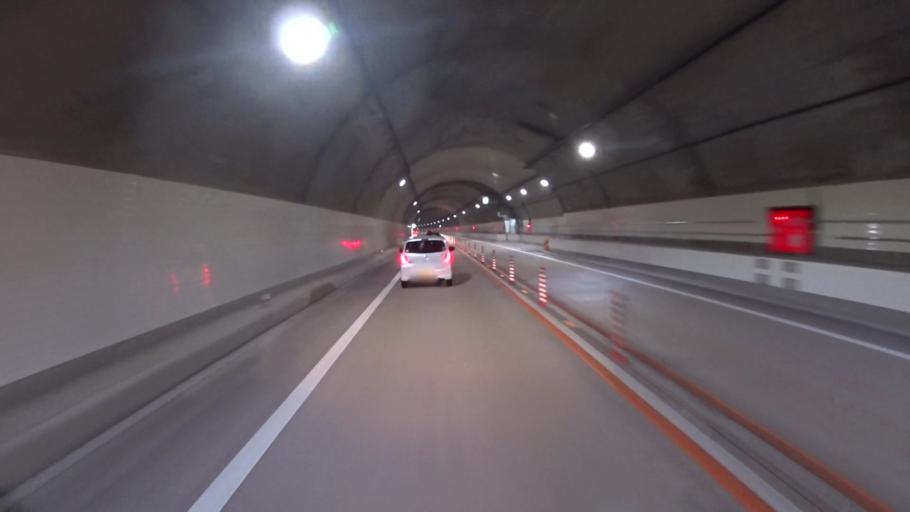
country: JP
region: Kyoto
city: Ayabe
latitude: 35.2313
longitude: 135.3451
